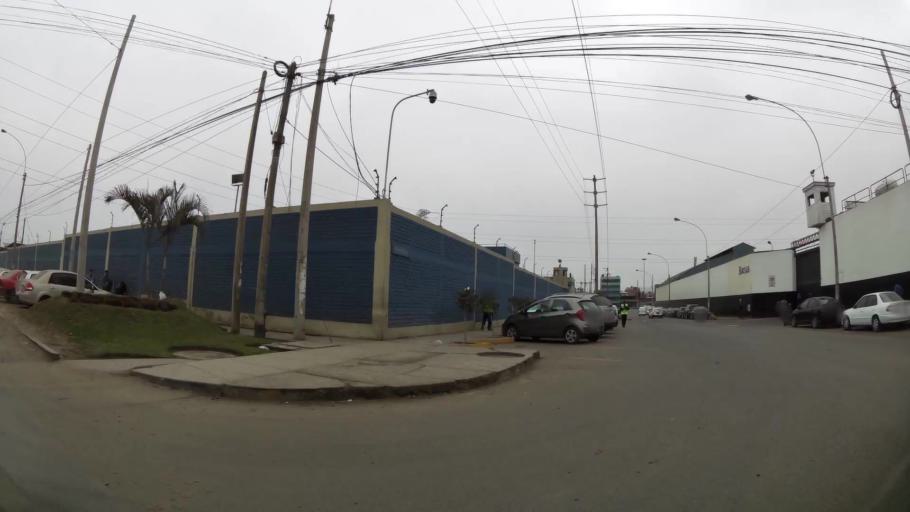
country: PE
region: Lima
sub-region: Lima
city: Surco
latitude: -12.1765
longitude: -76.9758
